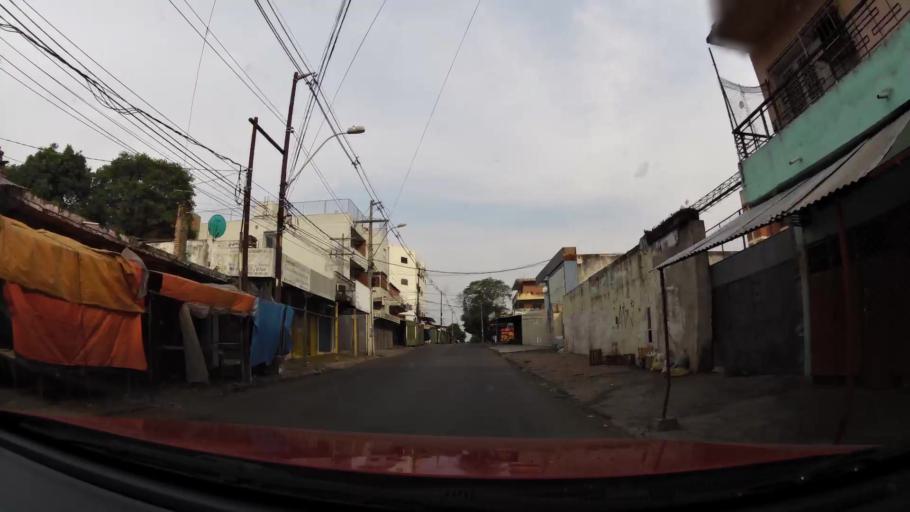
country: PY
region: Asuncion
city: Asuncion
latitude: -25.3007
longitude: -57.6248
